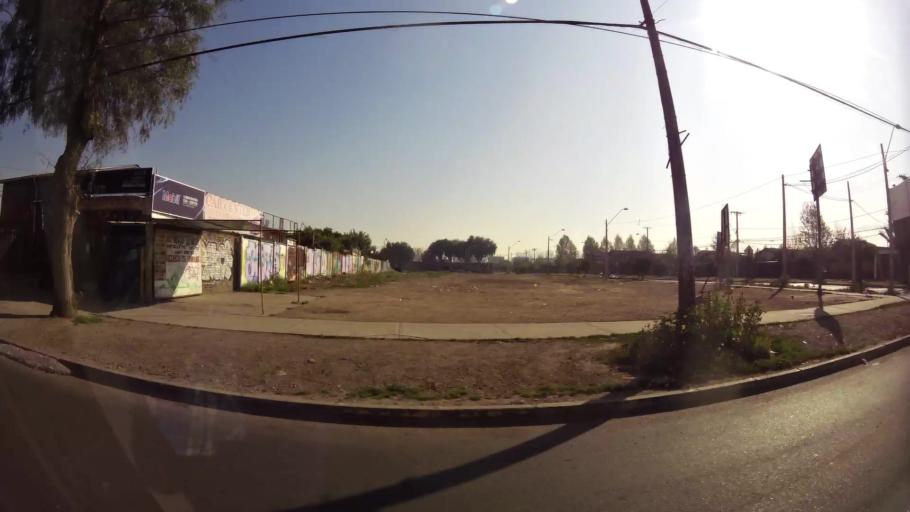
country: CL
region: Santiago Metropolitan
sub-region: Provincia de Santiago
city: Lo Prado
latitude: -33.4557
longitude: -70.7513
